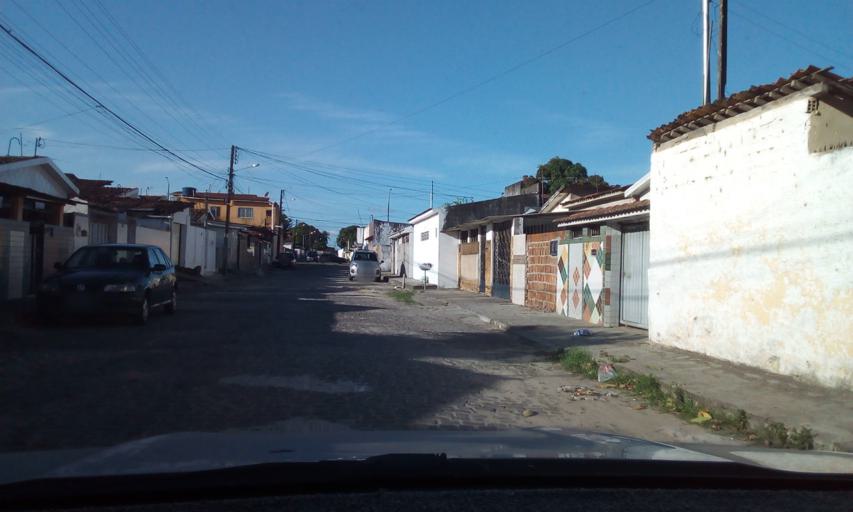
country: BR
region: Paraiba
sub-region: Bayeux
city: Bayeux
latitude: -7.1260
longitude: -34.9165
